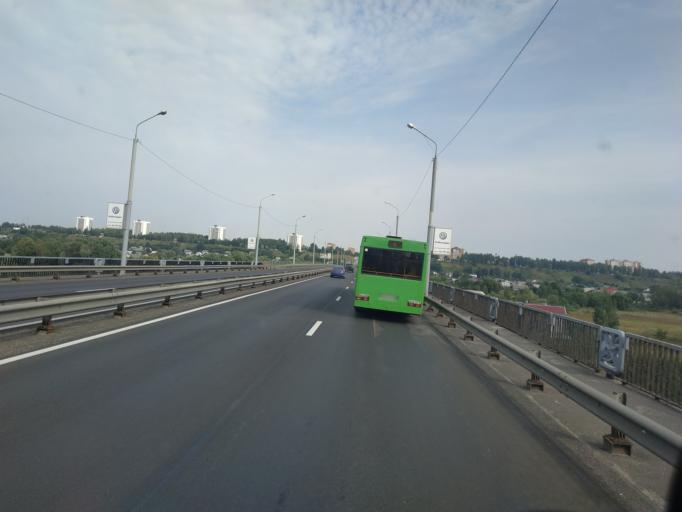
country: BY
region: Mogilev
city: Mahilyow
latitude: 53.8925
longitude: 30.3744
